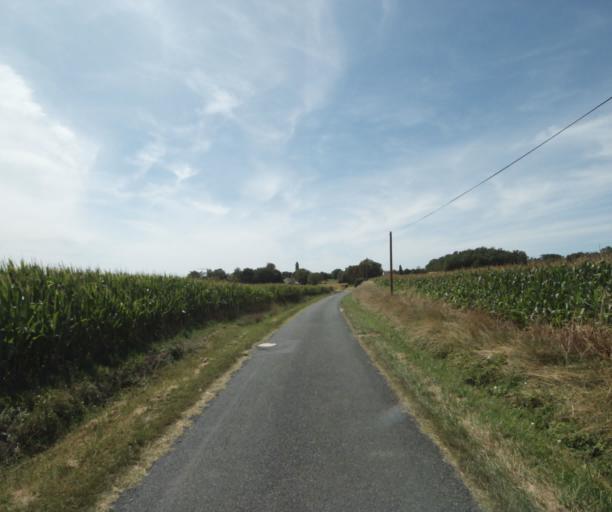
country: FR
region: Midi-Pyrenees
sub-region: Departement du Tarn
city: Puylaurens
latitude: 43.5256
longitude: 2.0150
